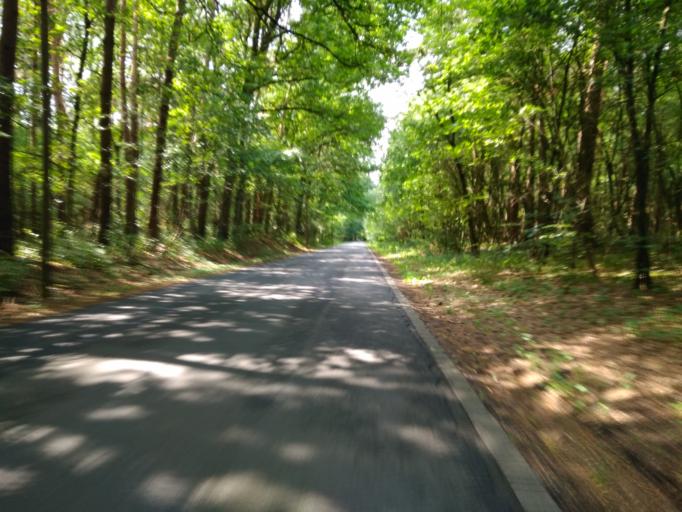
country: DE
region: North Rhine-Westphalia
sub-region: Regierungsbezirk Dusseldorf
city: Schermbeck
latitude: 51.6771
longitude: 6.8987
